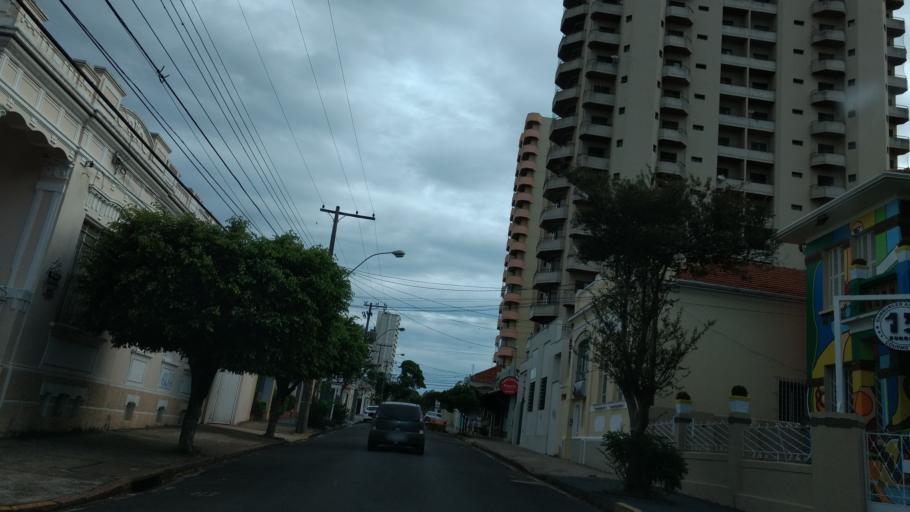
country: BR
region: Sao Paulo
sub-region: Botucatu
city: Botucatu
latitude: -22.8882
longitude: -48.4427
